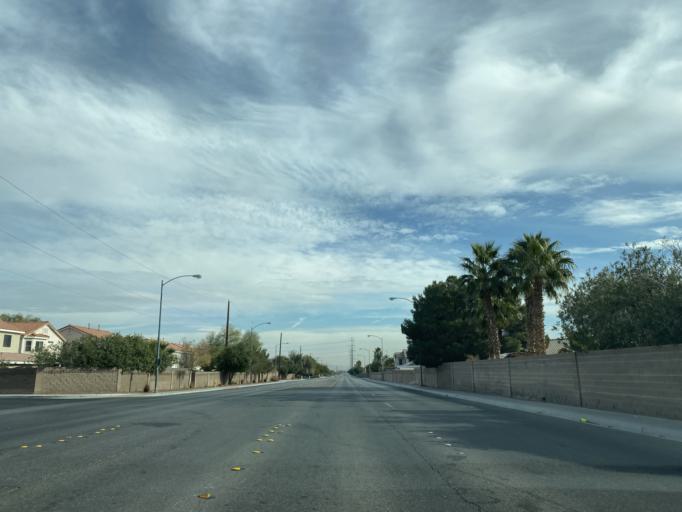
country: US
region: Nevada
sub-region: Clark County
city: North Las Vegas
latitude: 36.2469
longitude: -115.1283
